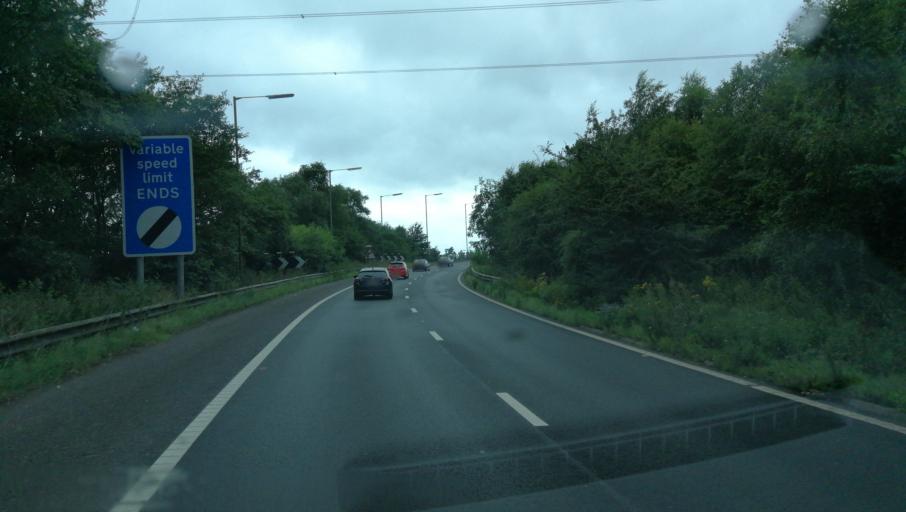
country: GB
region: England
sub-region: Manchester
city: Swinton
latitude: 53.5238
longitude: -2.3563
